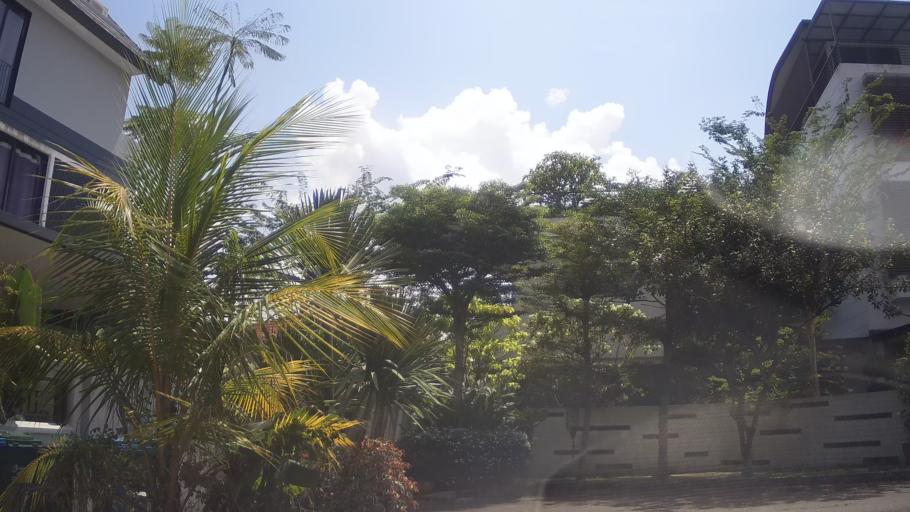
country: MY
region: Johor
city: Johor Bahru
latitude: 1.3670
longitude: 103.7691
